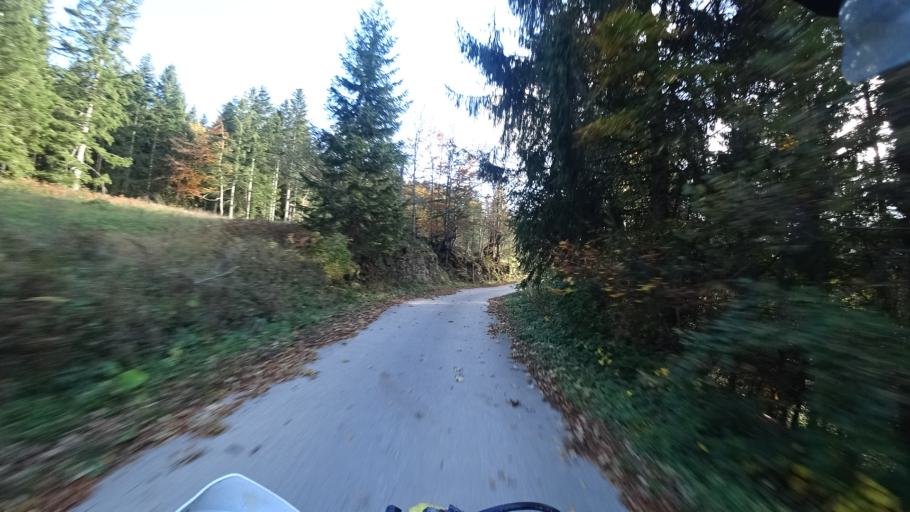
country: HR
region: Karlovacka
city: Plaski
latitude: 44.9779
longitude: 15.4014
